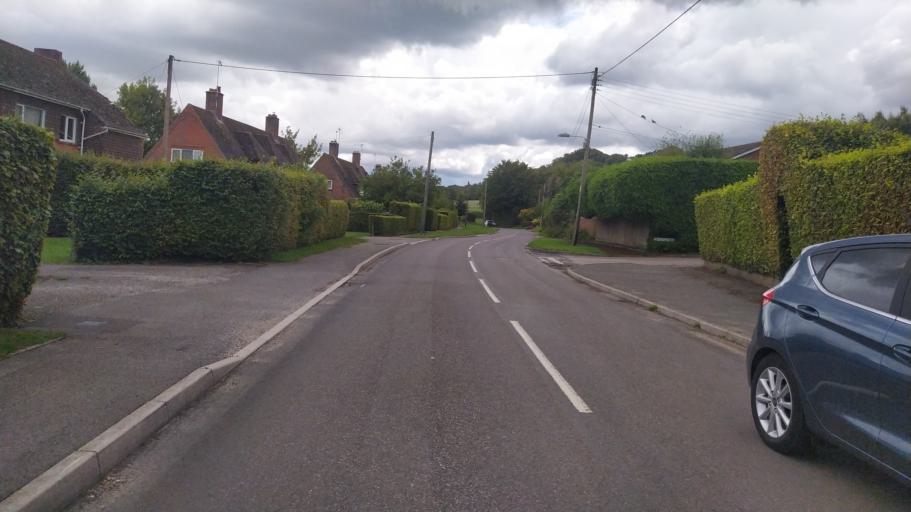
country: GB
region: England
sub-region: Dorset
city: Verwood
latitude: 50.9177
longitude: -1.9181
